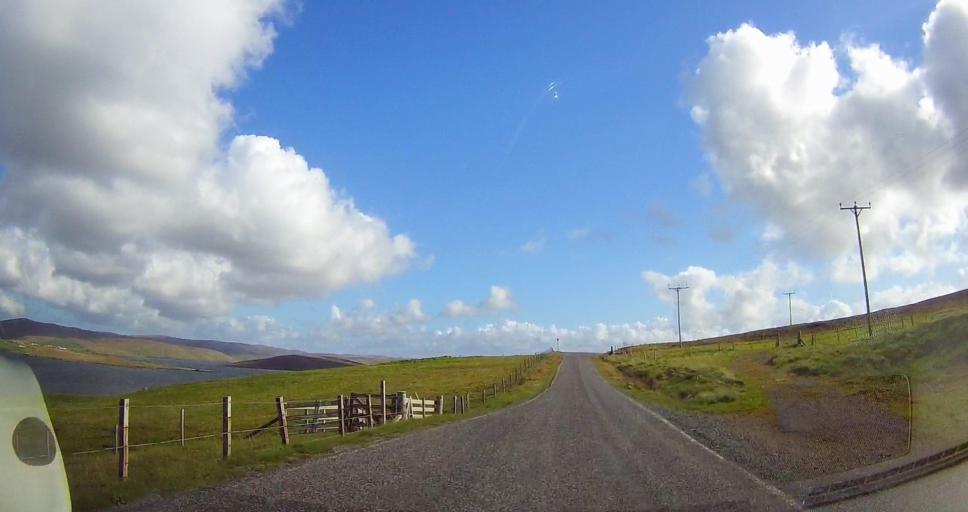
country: GB
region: Scotland
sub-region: Shetland Islands
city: Lerwick
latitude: 60.3825
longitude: -1.3790
